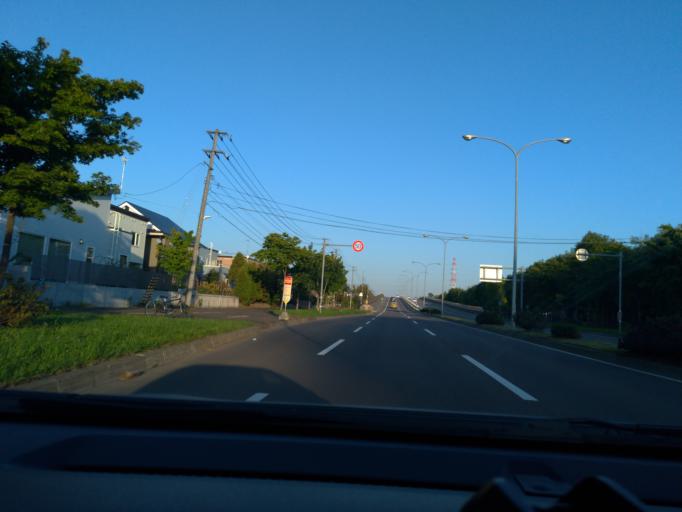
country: JP
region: Hokkaido
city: Ishikari
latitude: 43.1577
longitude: 141.4043
